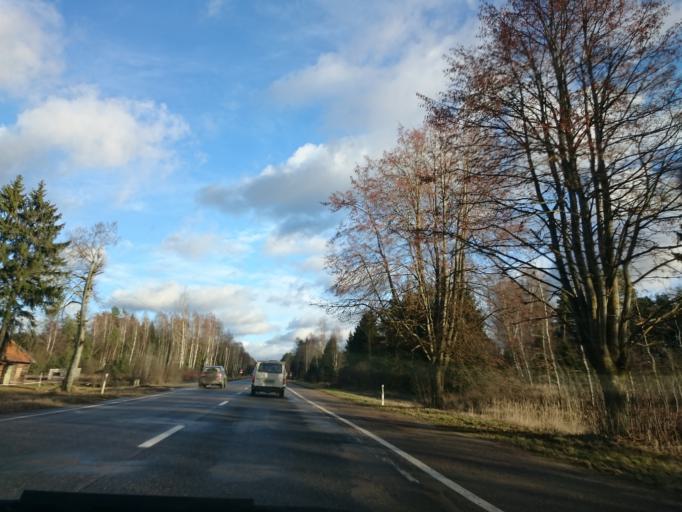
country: LV
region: Incukalns
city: Vangazi
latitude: 57.0943
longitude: 24.5682
